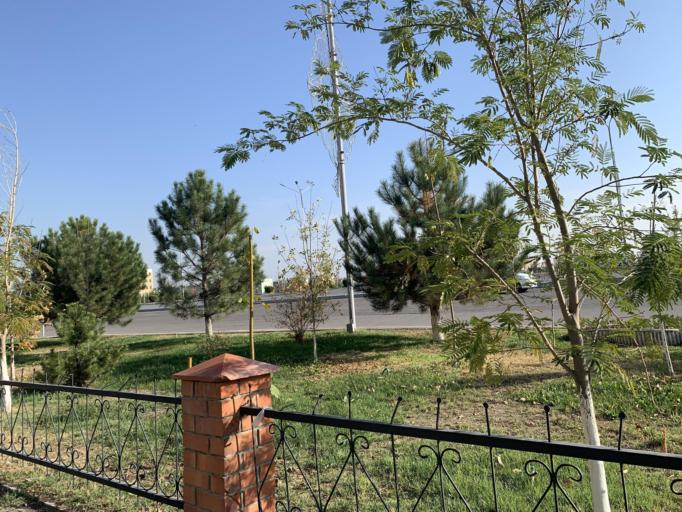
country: UZ
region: Namangan
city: Namangan Shahri
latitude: 40.9963
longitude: 71.5940
